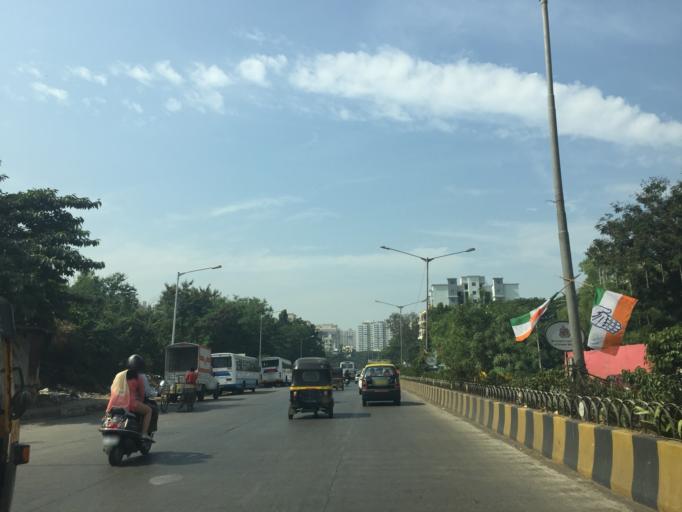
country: IN
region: Maharashtra
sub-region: Mumbai Suburban
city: Borivli
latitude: 19.2201
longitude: 72.8457
